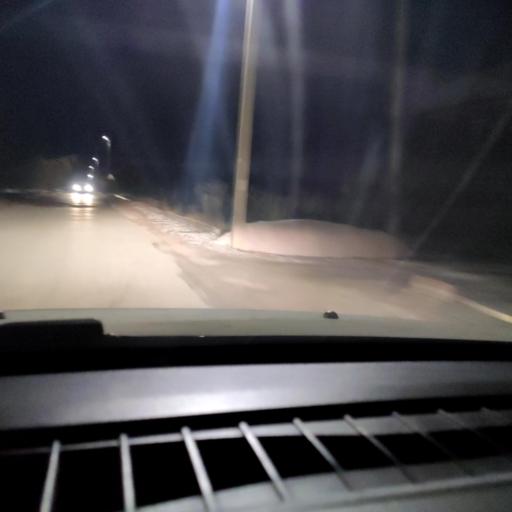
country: RU
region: Samara
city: Podstepki
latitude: 53.5180
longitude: 49.1737
